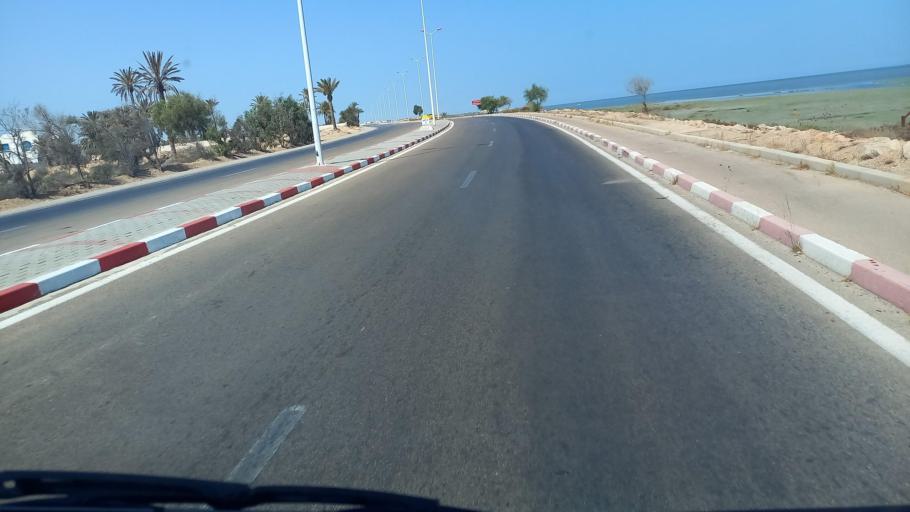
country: TN
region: Madanin
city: Houmt Souk
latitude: 33.8740
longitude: 10.9271
